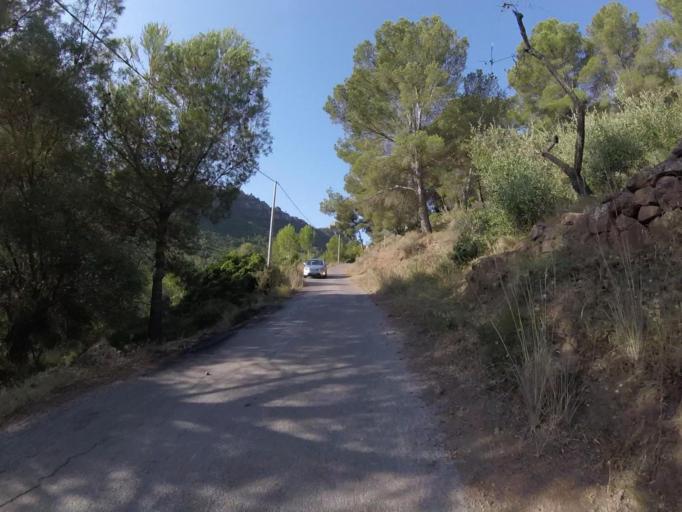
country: ES
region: Valencia
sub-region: Provincia de Castello
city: Benicassim
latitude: 40.0853
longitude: 0.0543
